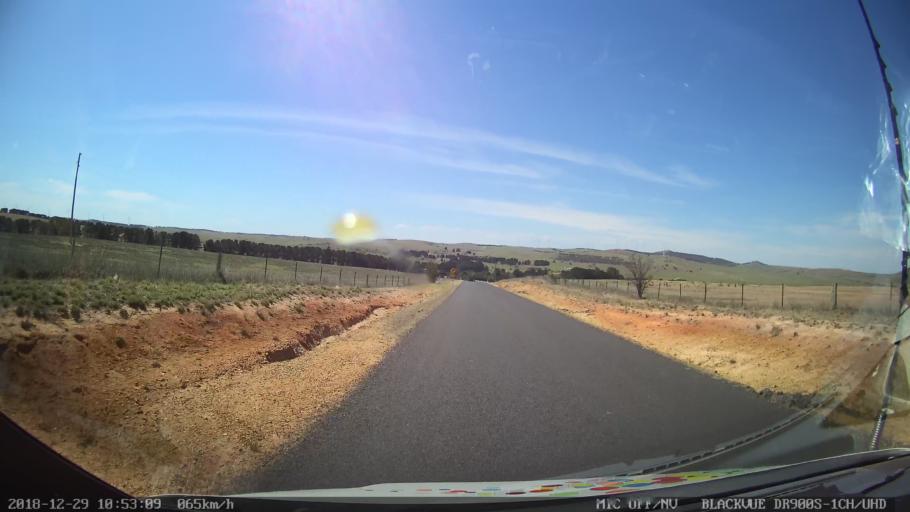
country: AU
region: New South Wales
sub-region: Palerang
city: Bungendore
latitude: -35.1057
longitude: 149.5211
